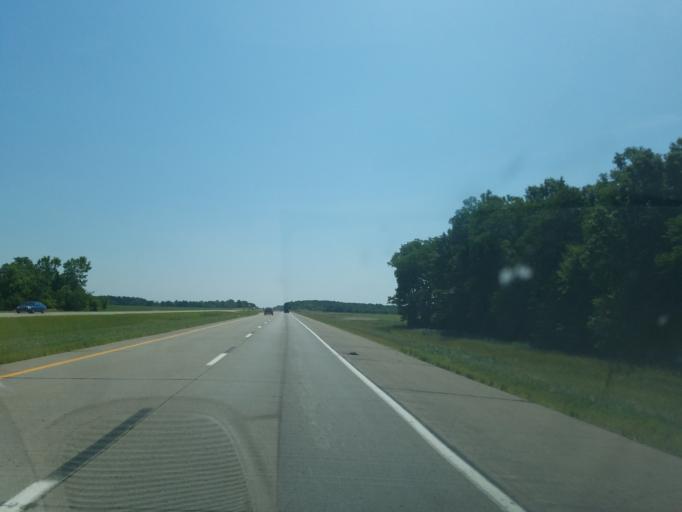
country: US
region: Ohio
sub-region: Allen County
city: Bluffton
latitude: 40.8275
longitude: -83.8887
